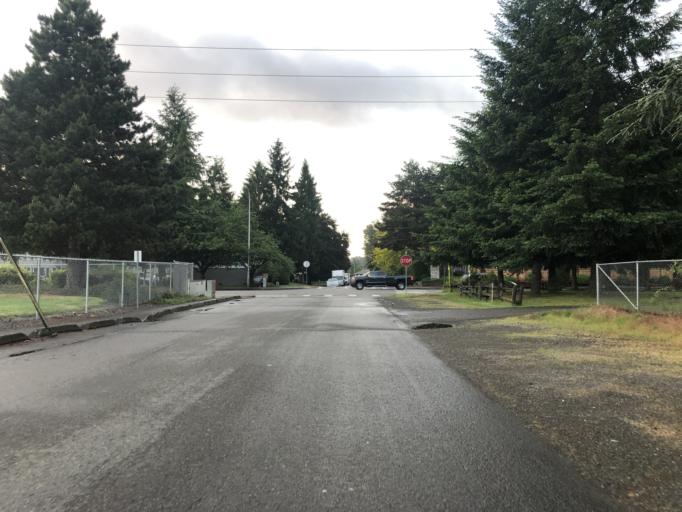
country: US
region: Washington
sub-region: King County
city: Auburn
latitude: 47.3146
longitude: -122.2096
